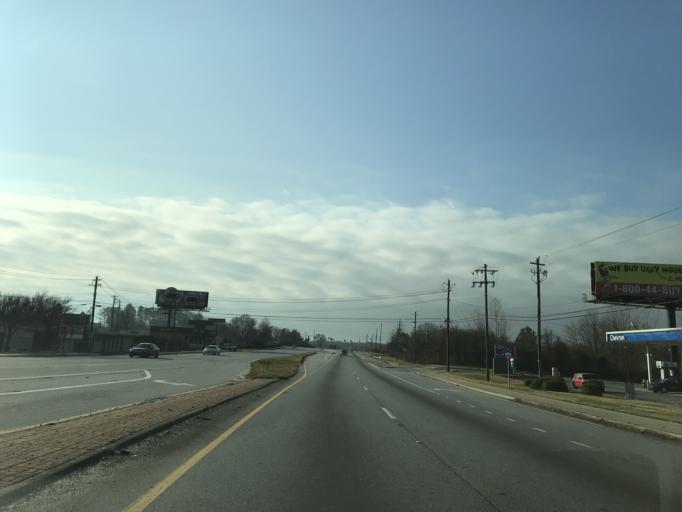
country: US
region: Georgia
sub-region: Clayton County
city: Forest Park
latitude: 33.6125
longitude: -84.4028
